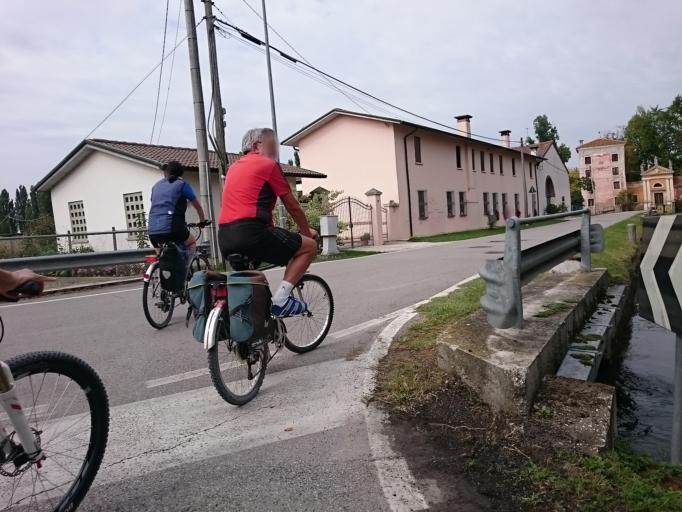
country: IT
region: Veneto
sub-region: Provincia di Padova
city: San Pietro in Gu
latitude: 45.6000
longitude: 11.6580
